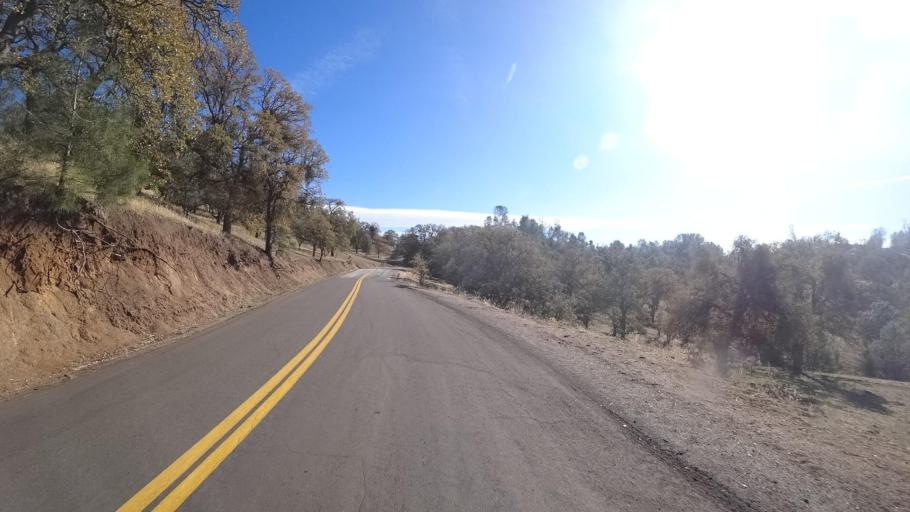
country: US
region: California
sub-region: Kern County
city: Bear Valley Springs
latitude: 35.3620
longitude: -118.5531
